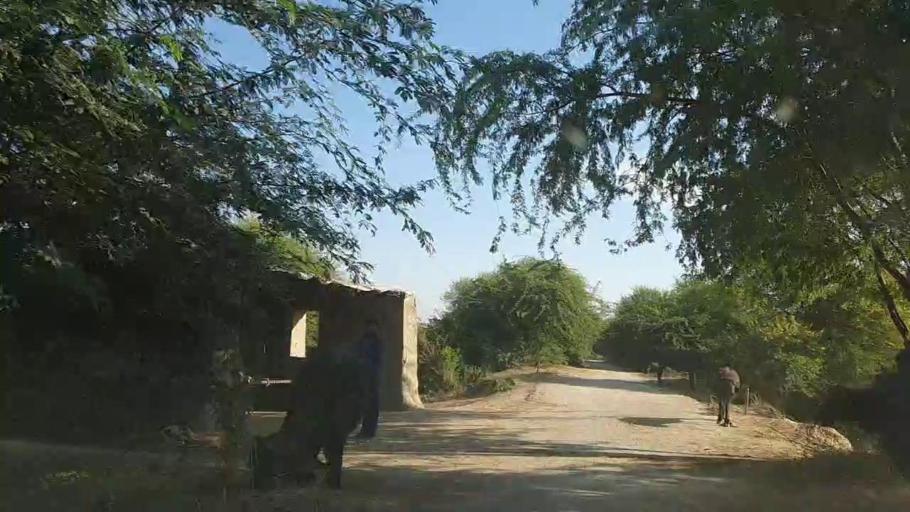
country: PK
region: Sindh
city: Bulri
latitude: 24.7850
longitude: 68.3504
